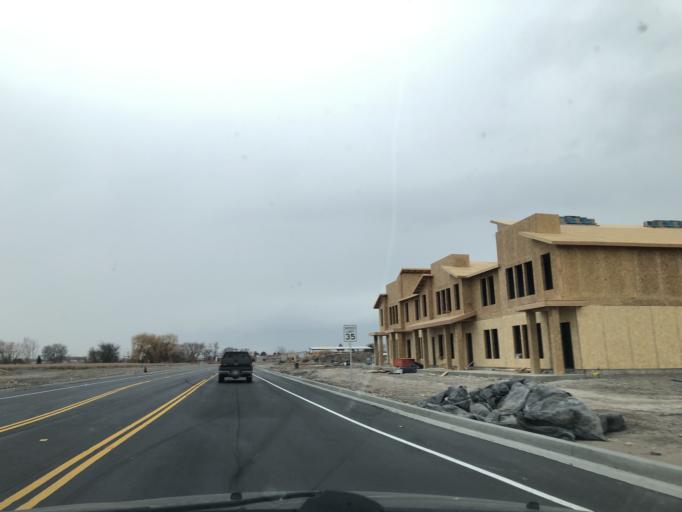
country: US
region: Utah
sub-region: Cache County
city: Nibley
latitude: 41.6930
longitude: -111.8590
